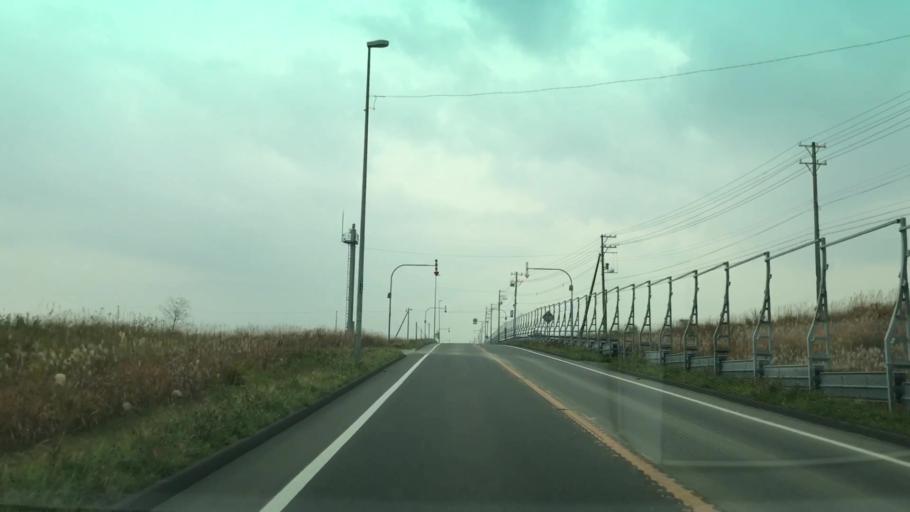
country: JP
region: Hokkaido
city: Ishikari
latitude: 43.3018
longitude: 141.4123
